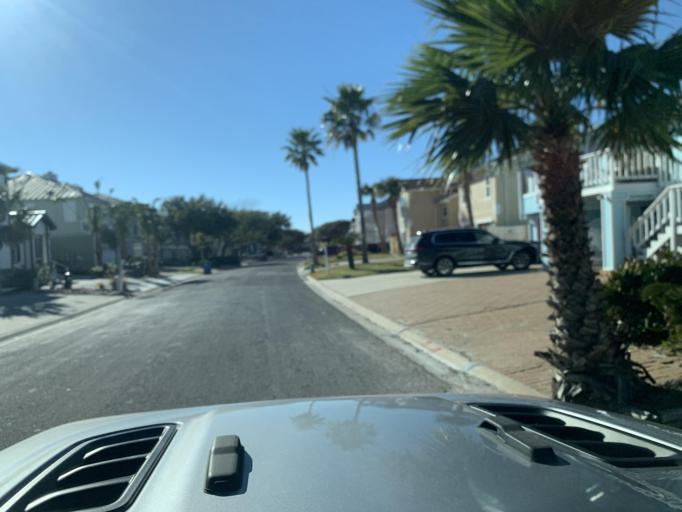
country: US
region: Texas
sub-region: Aransas County
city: Fulton
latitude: 28.0353
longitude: -97.0307
